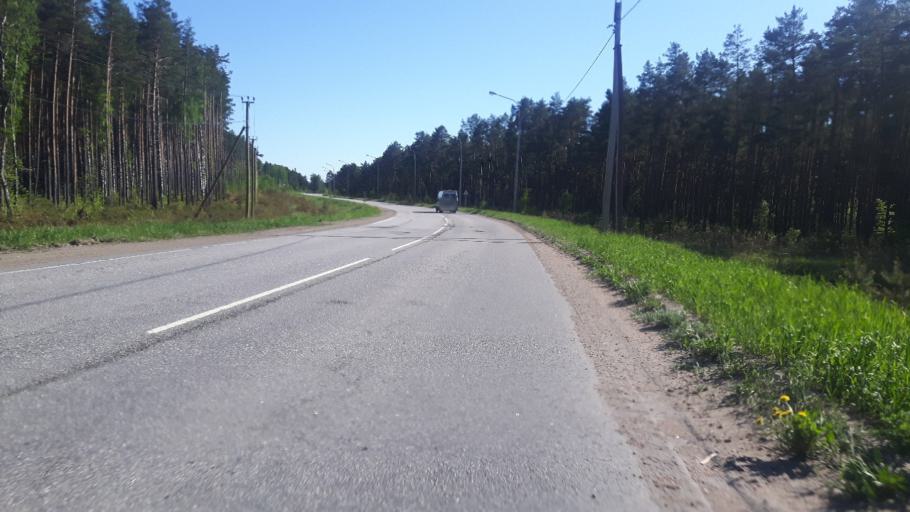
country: RU
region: Leningrad
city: Sosnovyy Bor
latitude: 60.2058
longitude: 29.0053
